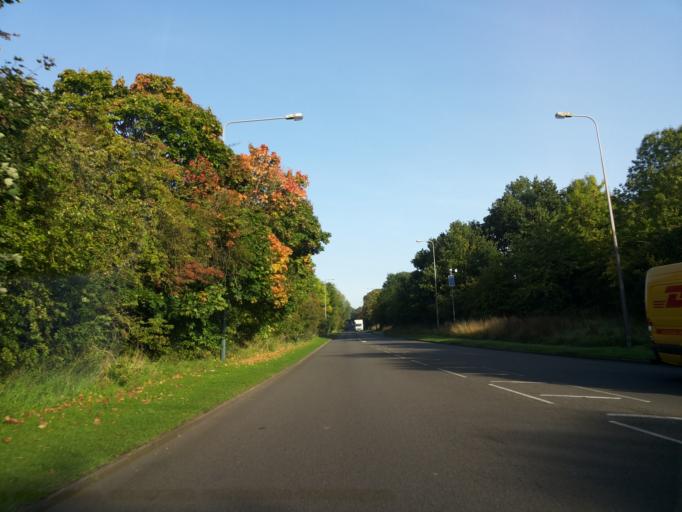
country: GB
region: England
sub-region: Solihull
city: Solihull
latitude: 52.4106
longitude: -1.7578
